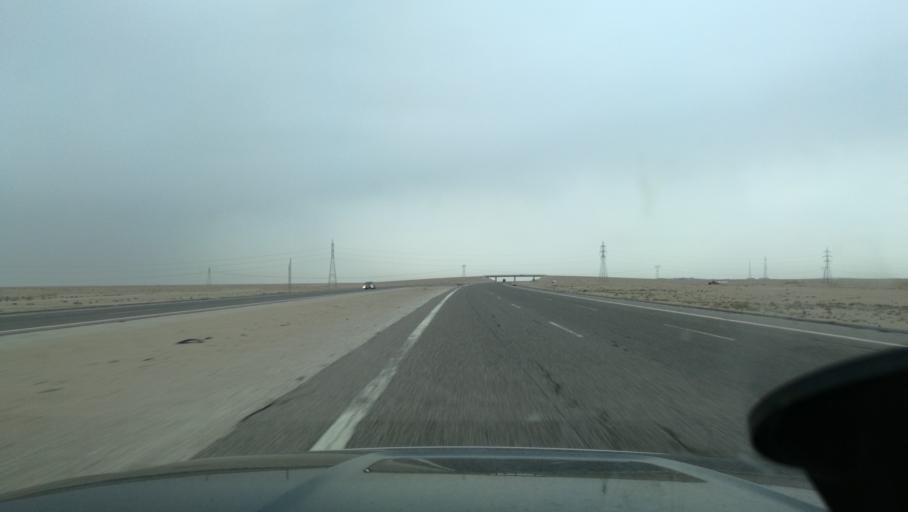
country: IQ
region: Dhi Qar
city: Suq ash Shuyukh
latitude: 30.6609
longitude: 46.5145
